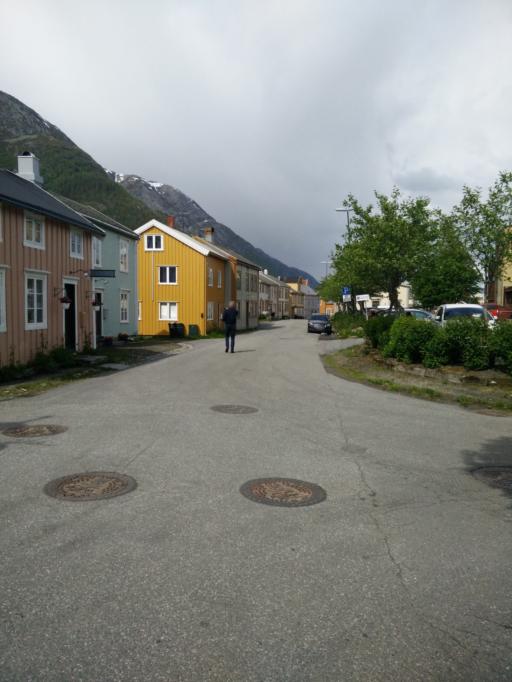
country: NO
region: Nordland
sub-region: Vefsn
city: Mosjoen
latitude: 65.8358
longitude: 13.1899
